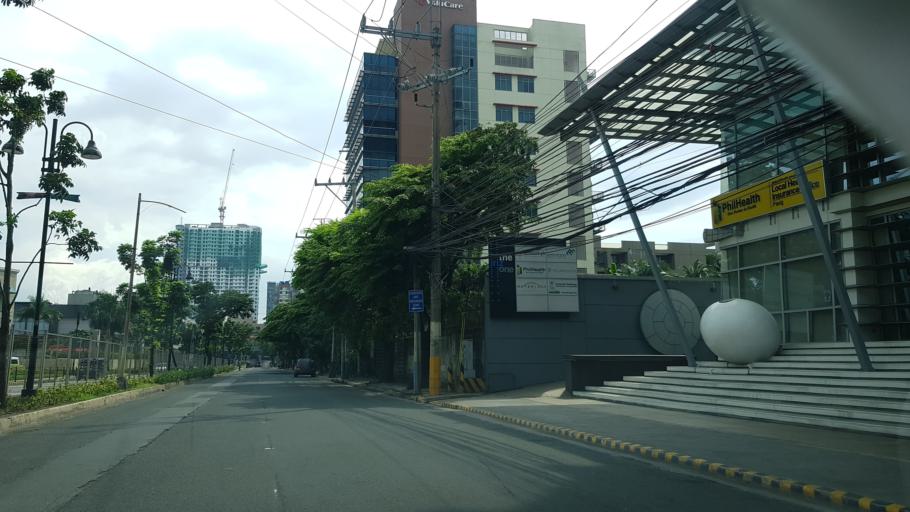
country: PH
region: Metro Manila
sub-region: Pasig
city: Pasig City
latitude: 14.5773
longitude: 121.0631
